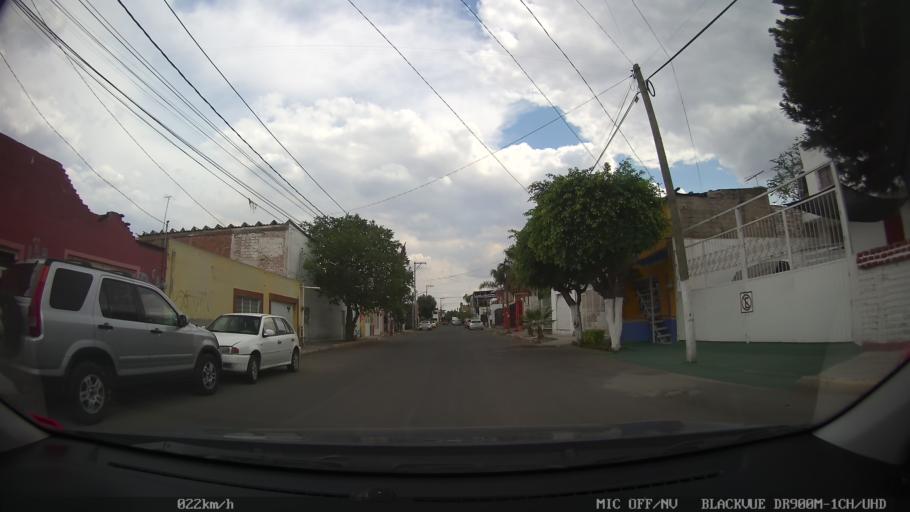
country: MX
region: Jalisco
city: Tlaquepaque
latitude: 20.6314
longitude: -103.2716
